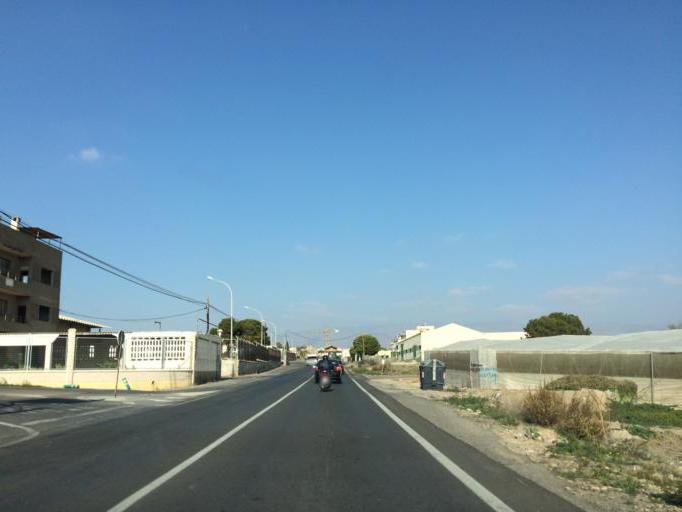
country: ES
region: Andalusia
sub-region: Provincia de Almeria
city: Viator
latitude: 36.8607
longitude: -2.4195
